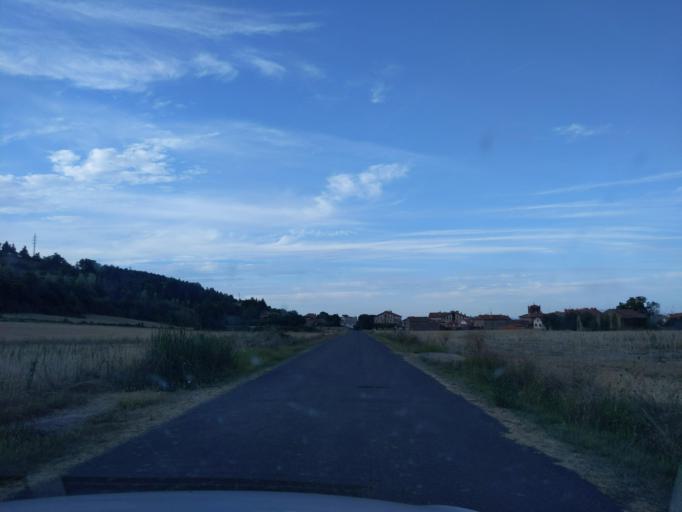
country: ES
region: La Rioja
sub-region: Provincia de La Rioja
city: Santurdejo
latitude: 42.3863
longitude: -2.9826
